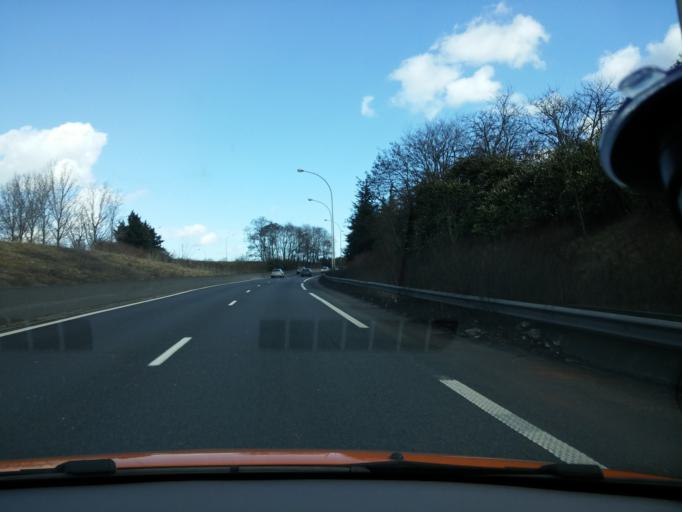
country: FR
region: Ile-de-France
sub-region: Departement du Val-de-Marne
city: Fresnes
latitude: 48.7548
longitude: 2.3344
